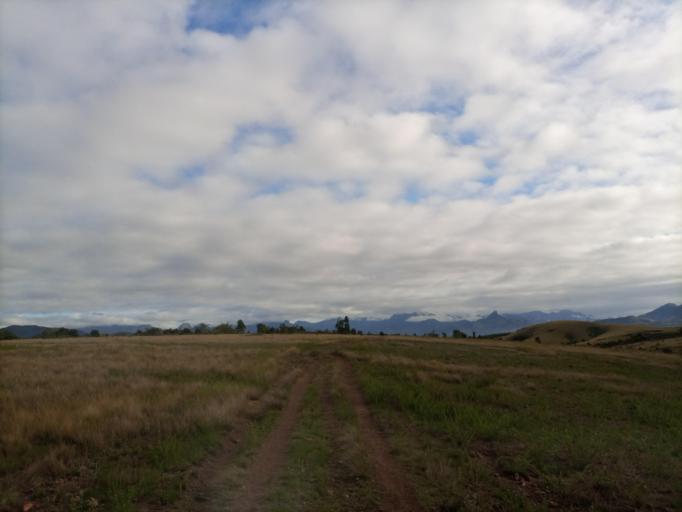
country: MG
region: Anosy
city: Fort Dauphin
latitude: -24.3115
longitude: 47.2507
